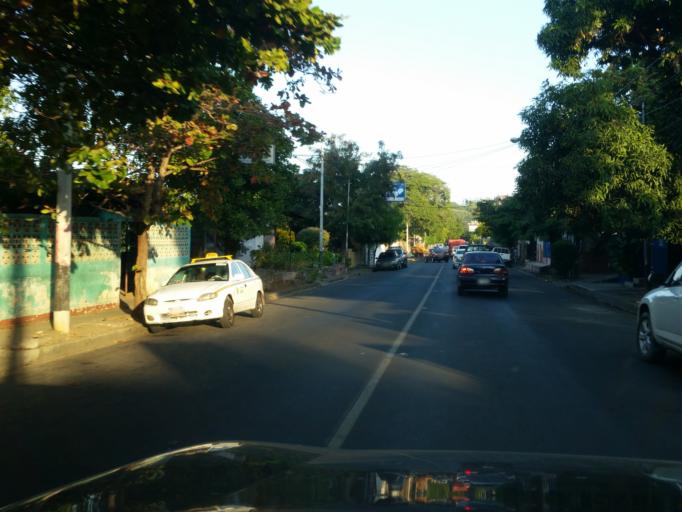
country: NI
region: Managua
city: Managua
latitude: 12.1425
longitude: -86.2839
